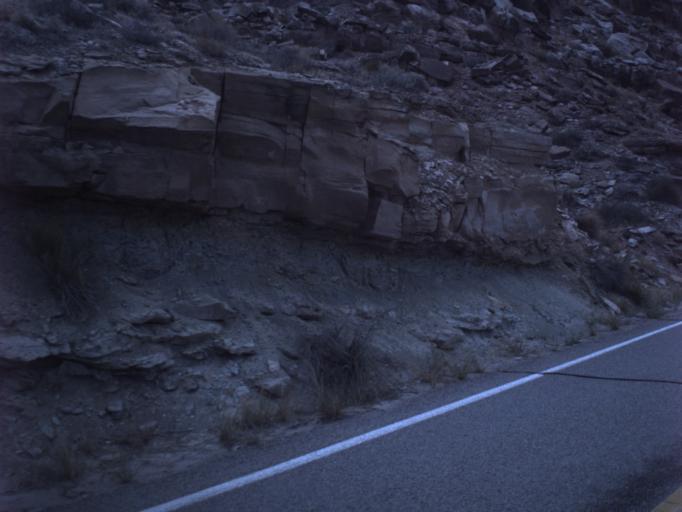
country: US
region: Utah
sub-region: Grand County
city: Moab
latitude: 38.8236
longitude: -109.2837
